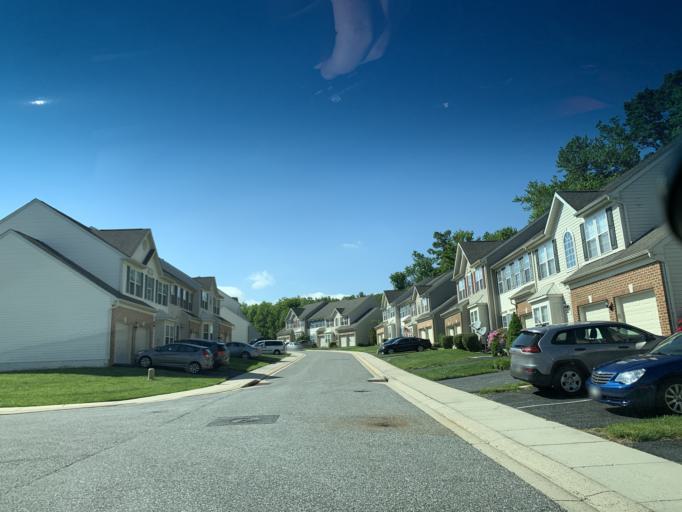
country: US
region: Maryland
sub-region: Harford County
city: Perryman
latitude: 39.4976
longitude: -76.2163
